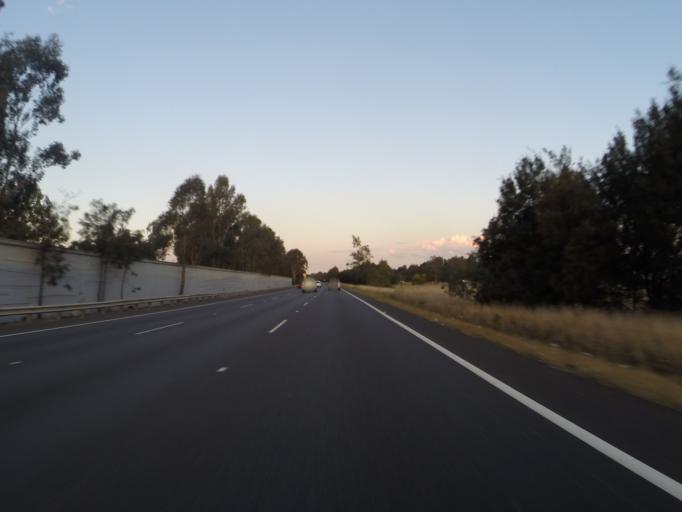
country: AU
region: New South Wales
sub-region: Penrith Municipality
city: Glenmore Park
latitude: -33.7810
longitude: 150.6853
